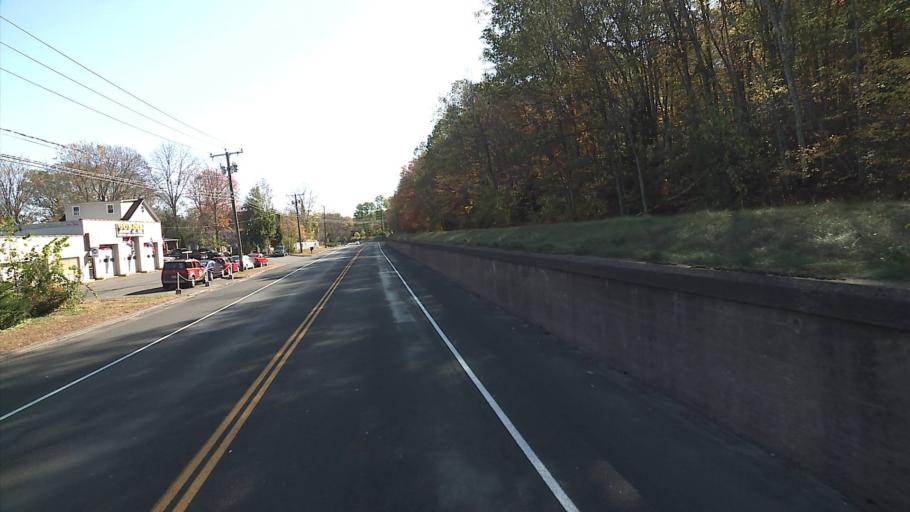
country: US
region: Connecticut
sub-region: Tolland County
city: Coventry Lake
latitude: 41.7399
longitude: -72.3766
